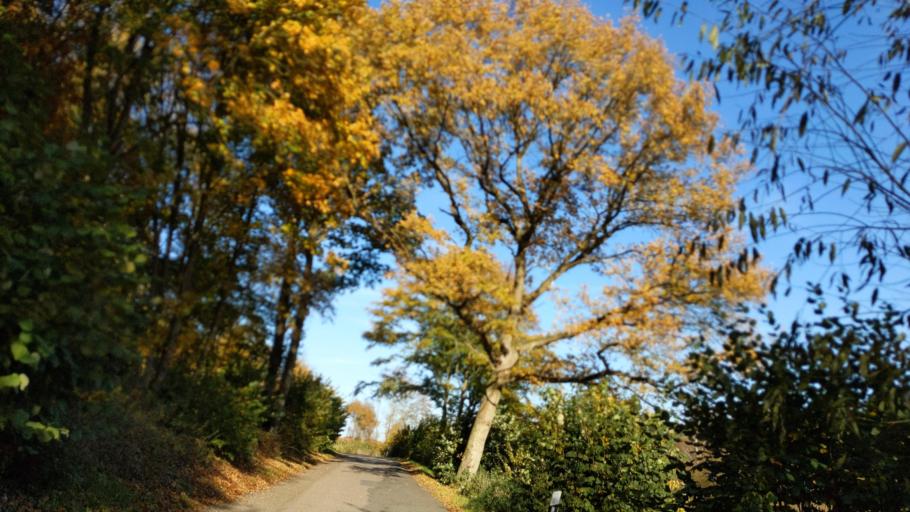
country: DE
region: Schleswig-Holstein
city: Kirchnuchel
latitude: 54.1534
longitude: 10.6619
